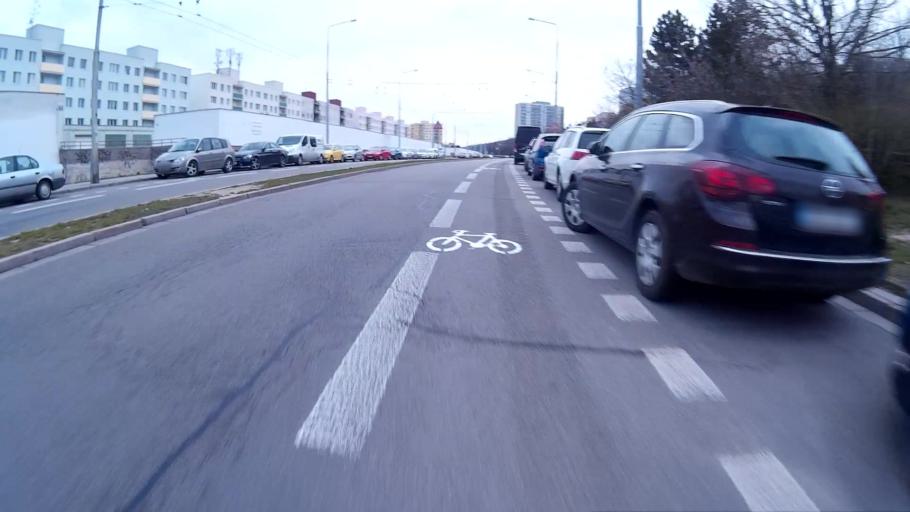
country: CZ
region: South Moravian
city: Ostopovice
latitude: 49.1767
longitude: 16.5578
